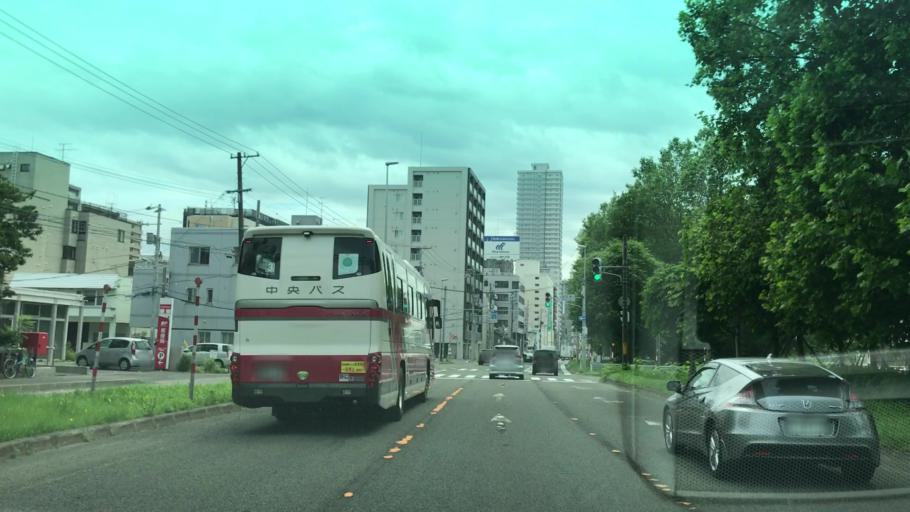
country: JP
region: Hokkaido
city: Sapporo
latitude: 43.0759
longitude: 141.3534
